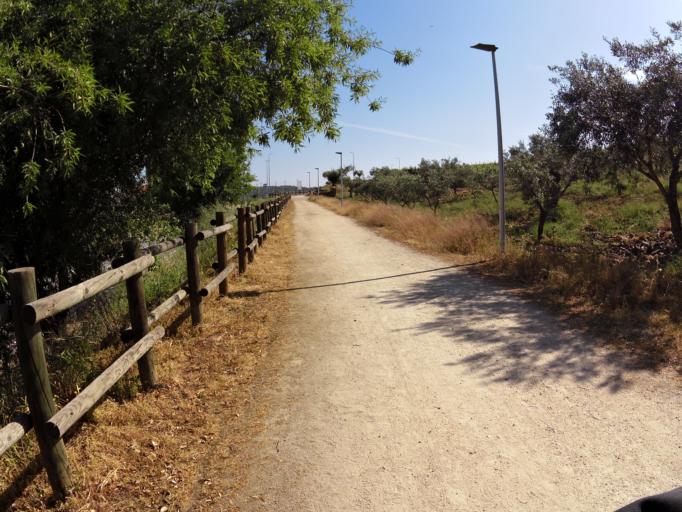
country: PT
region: Braganca
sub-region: Torre de Moncorvo
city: Torre de Moncorvo
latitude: 41.1777
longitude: -7.0388
